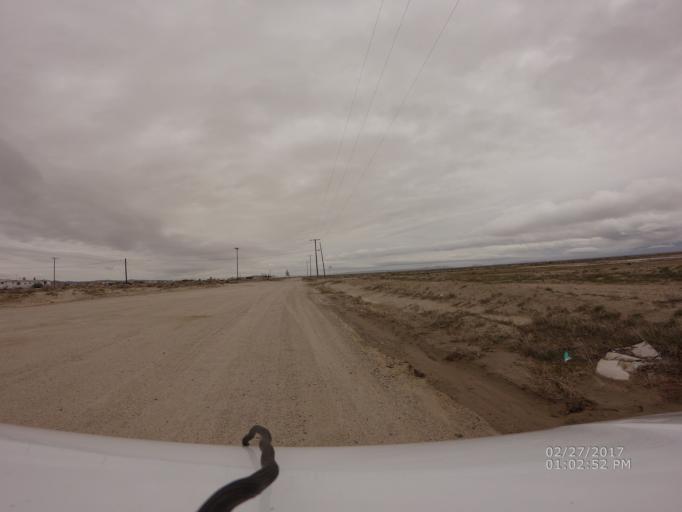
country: US
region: California
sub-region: Kern County
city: Rosamond
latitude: 34.8207
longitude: -118.1496
